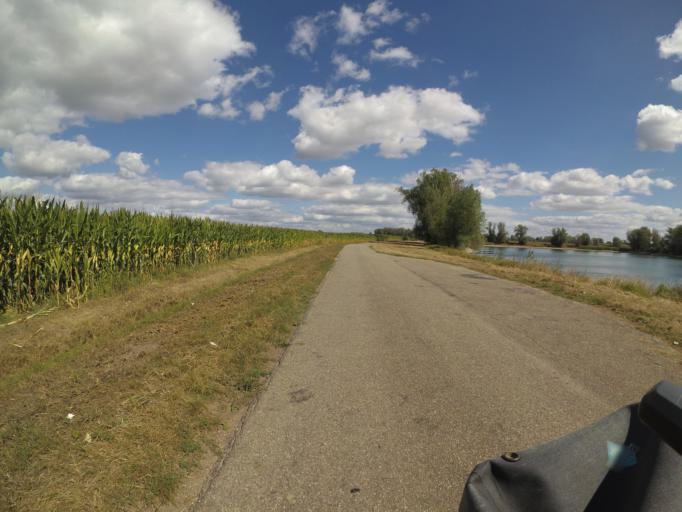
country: NL
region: Gelderland
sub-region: Gemeente Buren
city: Lienden
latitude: 51.8970
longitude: 5.5086
